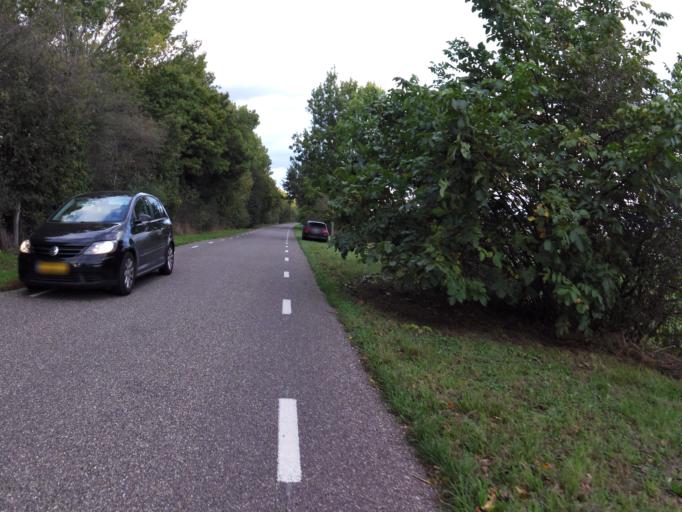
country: NL
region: Limburg
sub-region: Gemeente Leudal
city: Haelen
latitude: 51.1857
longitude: 5.9283
